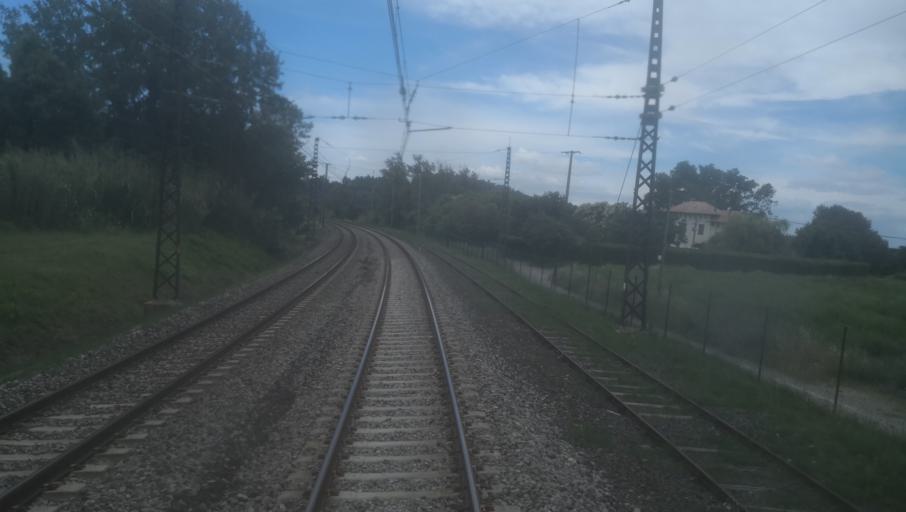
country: FR
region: Languedoc-Roussillon
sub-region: Departement de l'Herault
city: Colombiers
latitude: 43.3173
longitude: 3.1349
